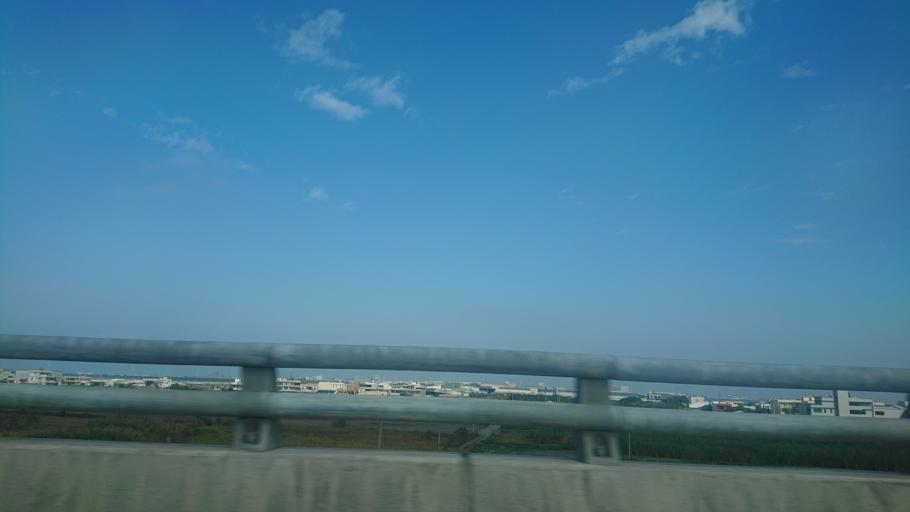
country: TW
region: Taiwan
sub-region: Changhua
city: Chang-hua
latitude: 24.0393
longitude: 120.4000
